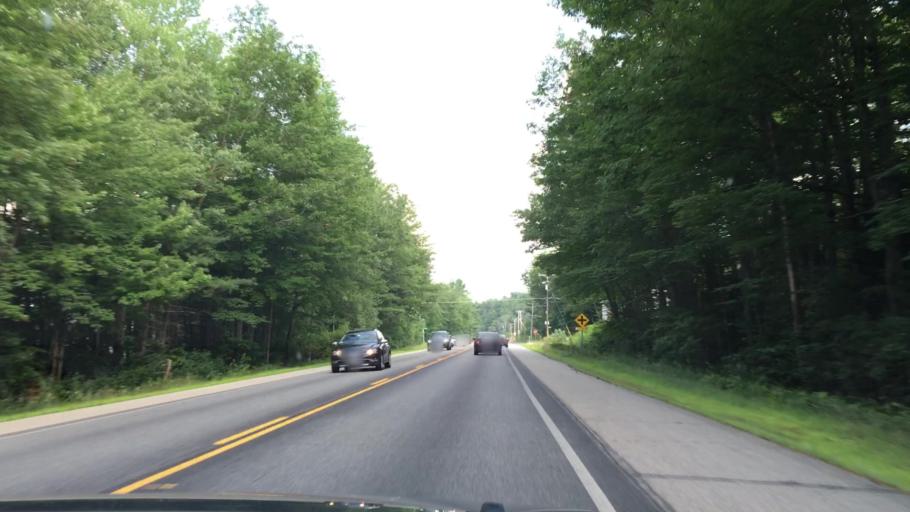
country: US
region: New Hampshire
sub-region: Strafford County
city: Farmington
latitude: 43.3895
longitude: -71.0872
